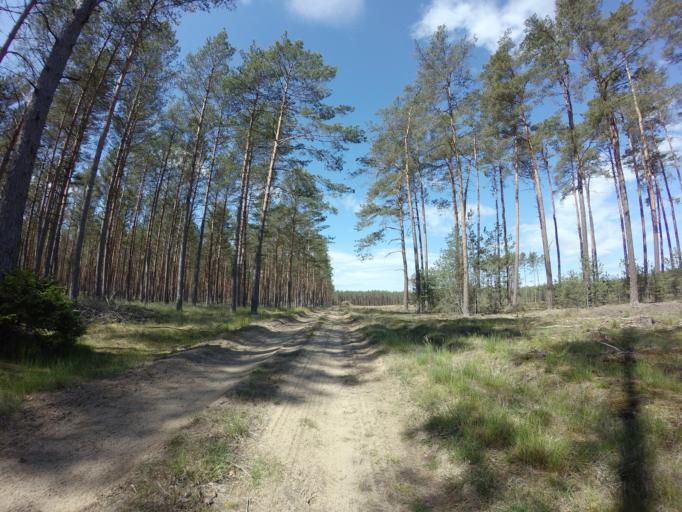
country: PL
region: West Pomeranian Voivodeship
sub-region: Powiat drawski
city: Kalisz Pomorski
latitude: 53.1786
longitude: 15.9527
